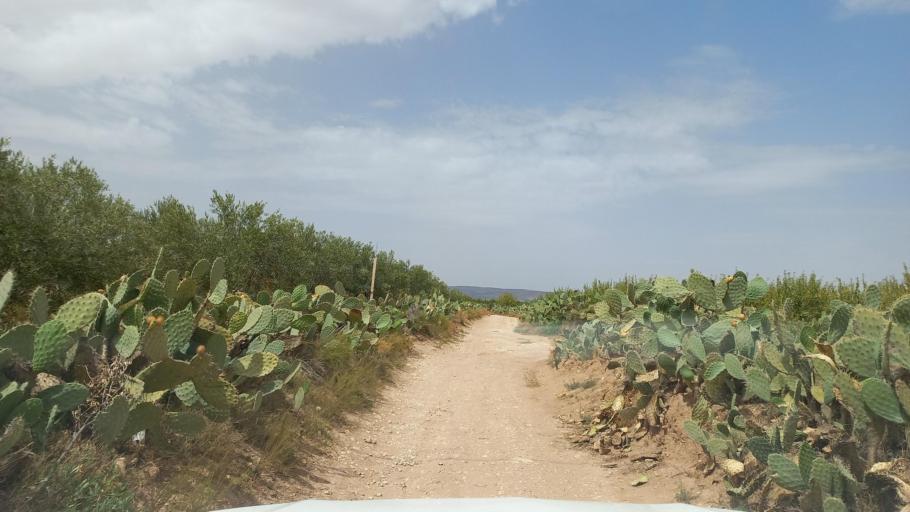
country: TN
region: Al Qasrayn
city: Kasserine
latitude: 35.2850
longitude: 9.0083
